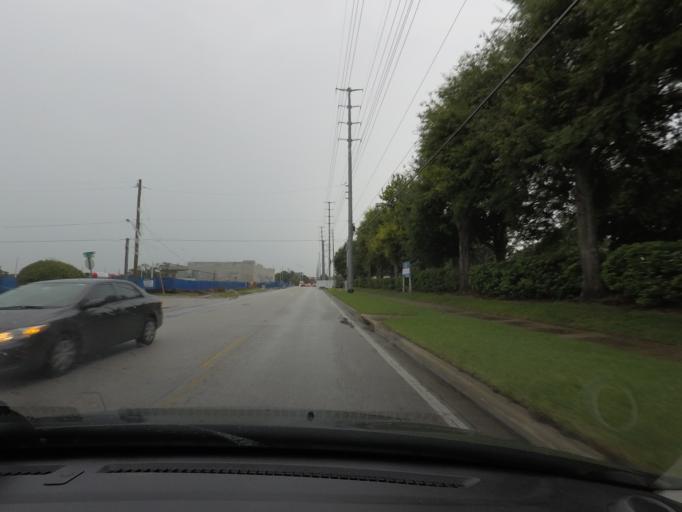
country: US
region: Florida
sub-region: Orange County
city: Holden Heights
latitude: 28.5094
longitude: -81.3738
